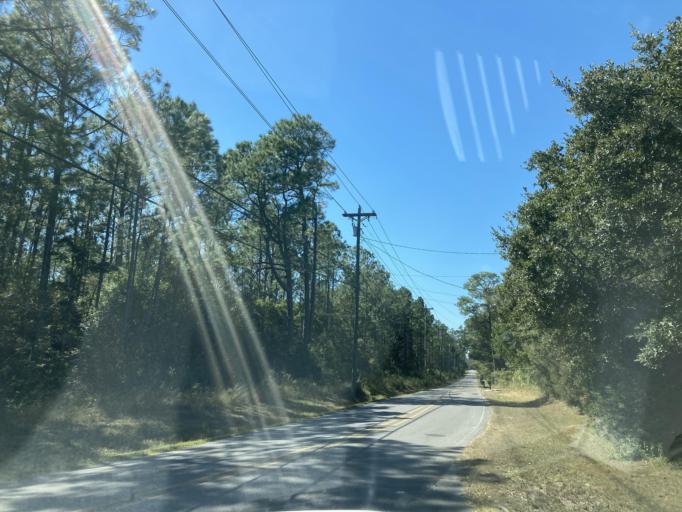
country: US
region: Mississippi
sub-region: Jackson County
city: Saint Martin
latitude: 30.4613
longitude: -88.8709
